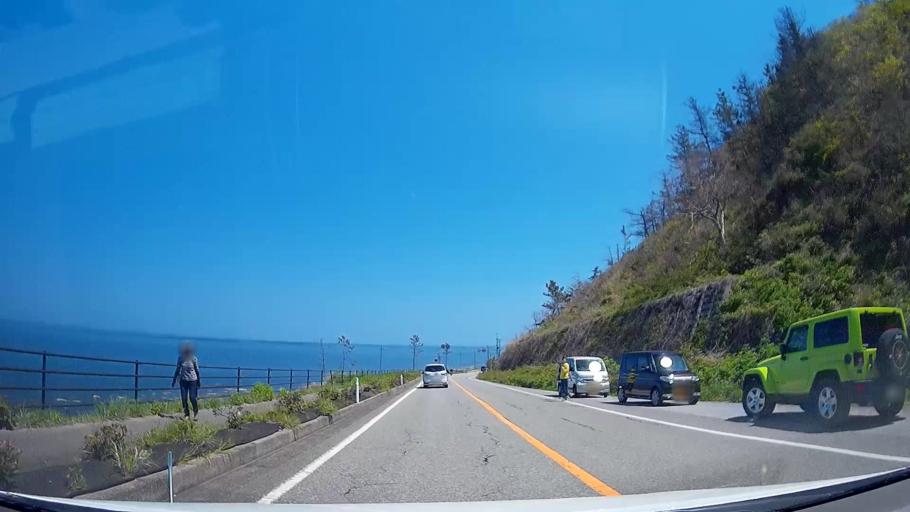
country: JP
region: Ishikawa
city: Nanao
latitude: 37.4270
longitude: 137.0032
